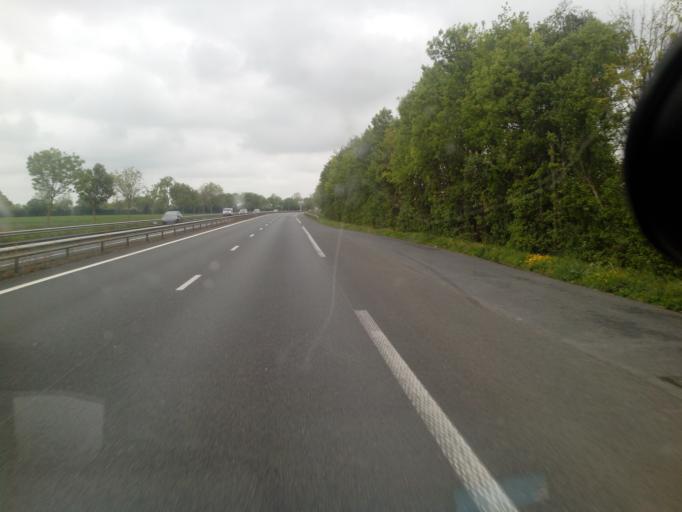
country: FR
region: Lower Normandy
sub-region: Departement du Calvados
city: Grainville-sur-Odon
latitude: 49.1347
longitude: -0.5594
